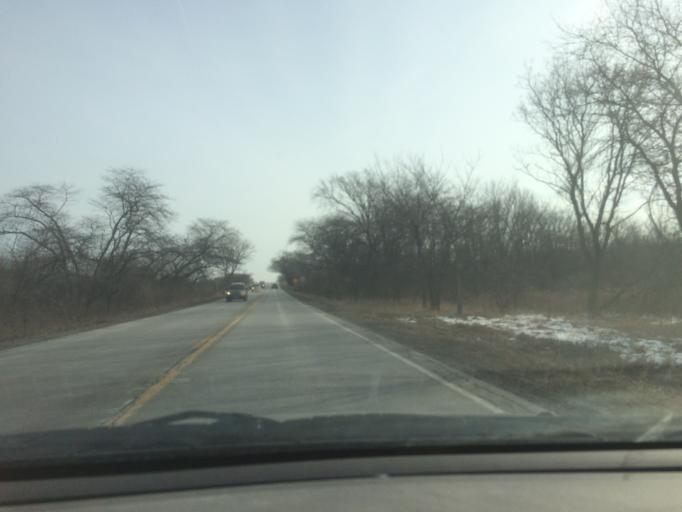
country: US
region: Illinois
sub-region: Cook County
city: Streamwood
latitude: 42.0464
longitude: -88.1521
